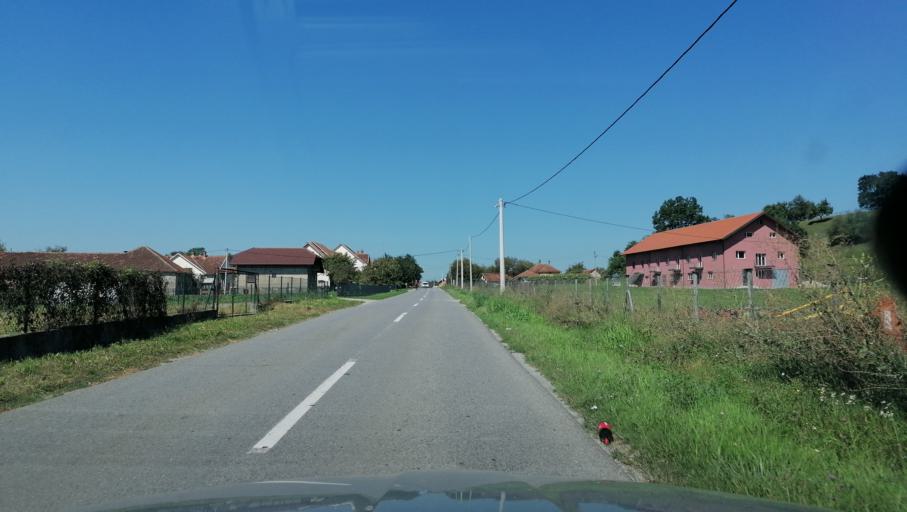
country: RS
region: Central Serbia
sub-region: Raski Okrug
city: Vrnjacka Banja
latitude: 43.6862
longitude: 20.8785
